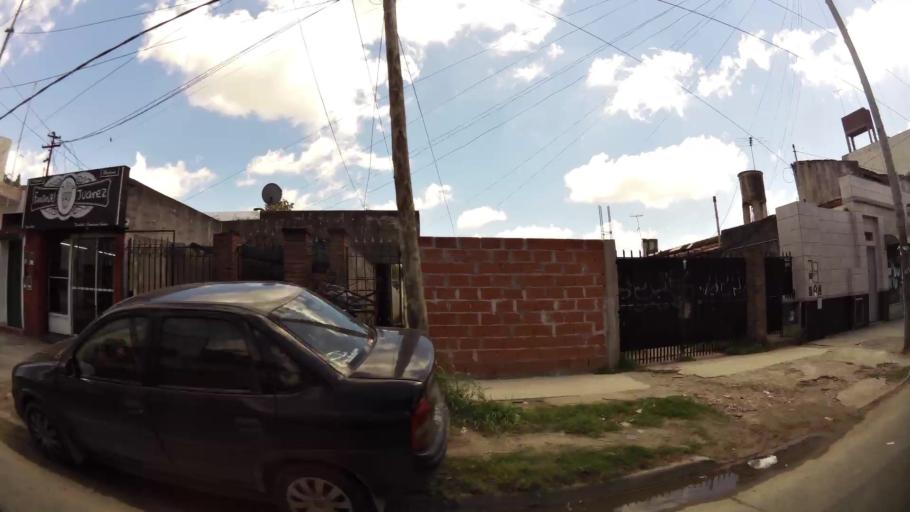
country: AR
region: Buenos Aires
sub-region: Partido de Lanus
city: Lanus
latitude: -34.6978
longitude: -58.4275
